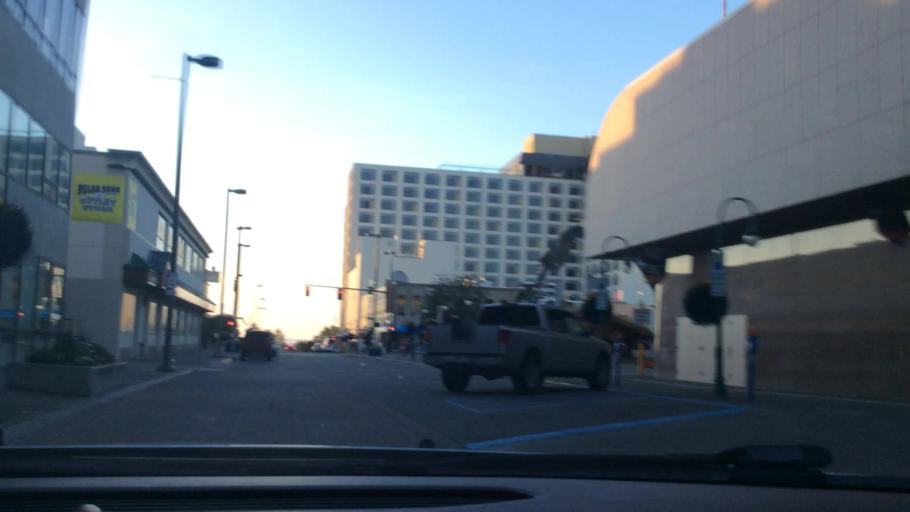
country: US
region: Alaska
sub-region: Anchorage Municipality
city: Anchorage
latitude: 61.2177
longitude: -149.8935
